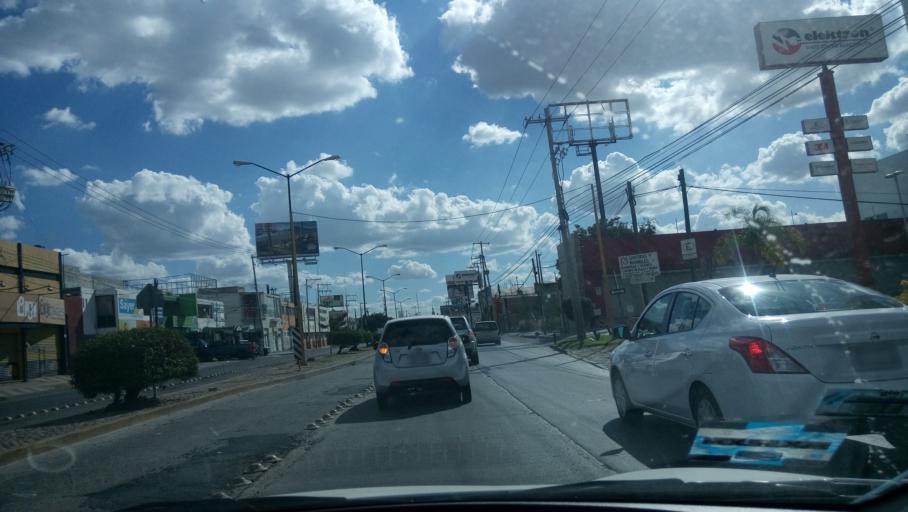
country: MX
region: Guanajuato
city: Leon
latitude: 21.1383
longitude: -101.6760
